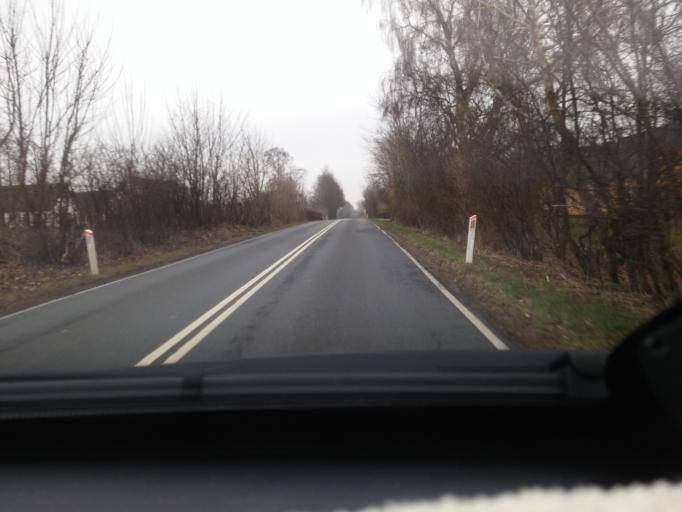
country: DK
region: South Denmark
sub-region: Kerteminde Kommune
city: Kerteminde
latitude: 55.4033
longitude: 10.7284
